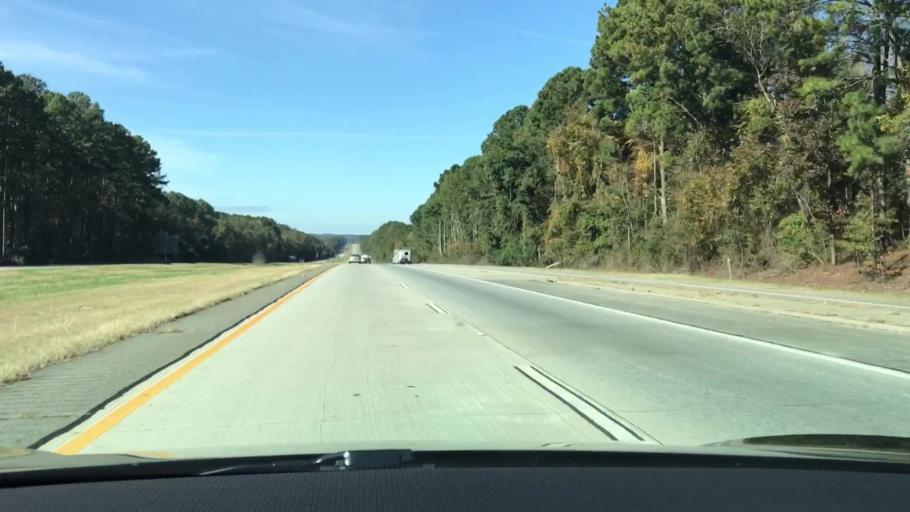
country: US
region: Georgia
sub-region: Greene County
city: Union Point
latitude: 33.5446
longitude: -83.0841
